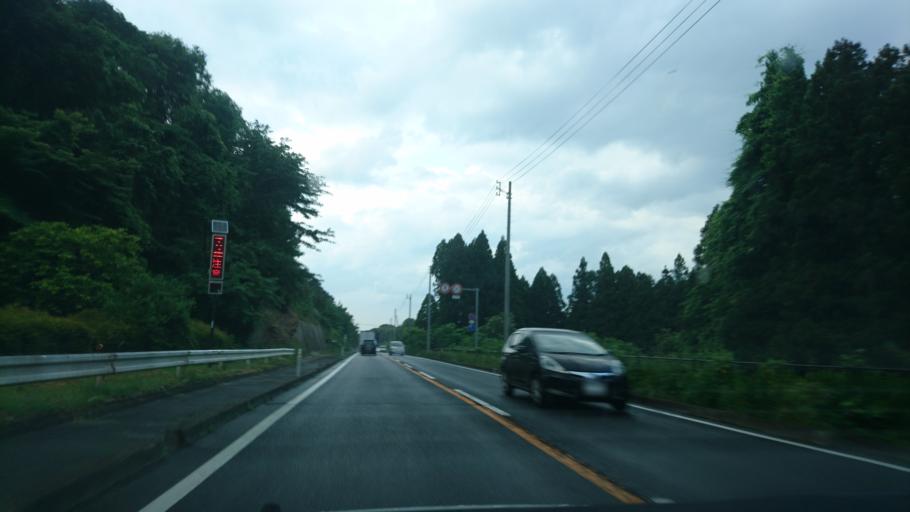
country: JP
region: Iwate
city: Ichinoseki
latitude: 38.9531
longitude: 141.1216
